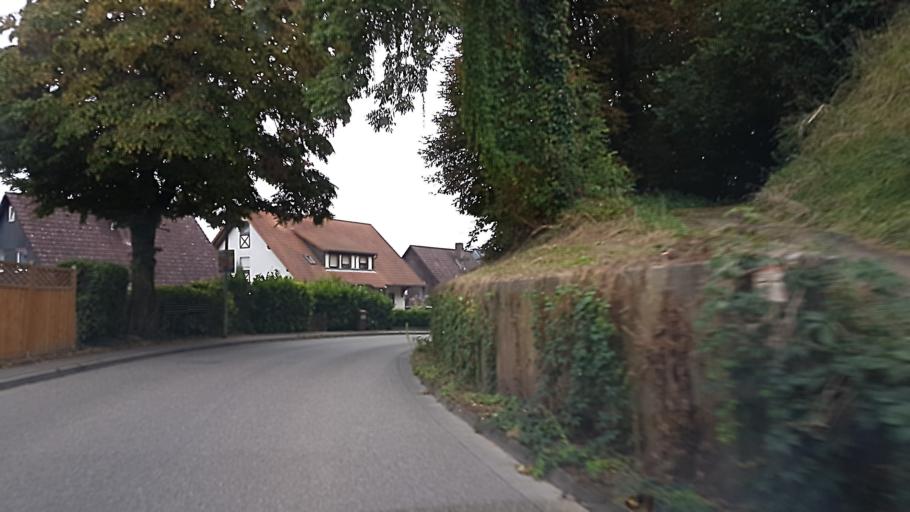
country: DE
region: Baden-Wuerttemberg
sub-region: Freiburg Region
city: Gottenheim
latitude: 48.0111
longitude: 7.7243
